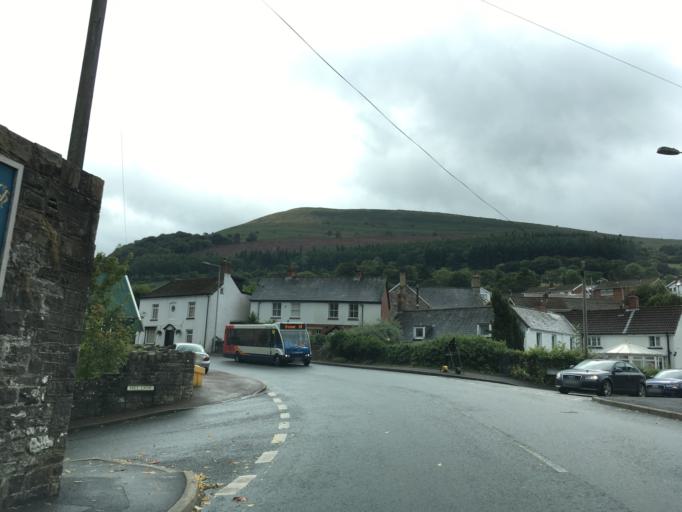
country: GB
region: Wales
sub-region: Monmouthshire
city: Gilwern
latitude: 51.8191
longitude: -3.0675
